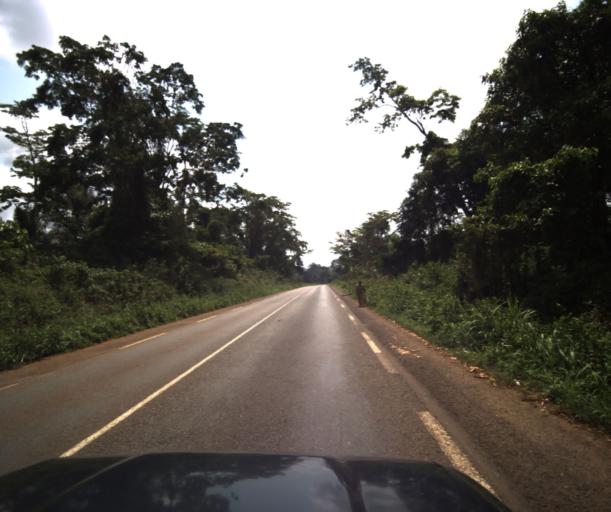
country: CM
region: Centre
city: Eseka
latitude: 3.8899
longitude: 10.7941
